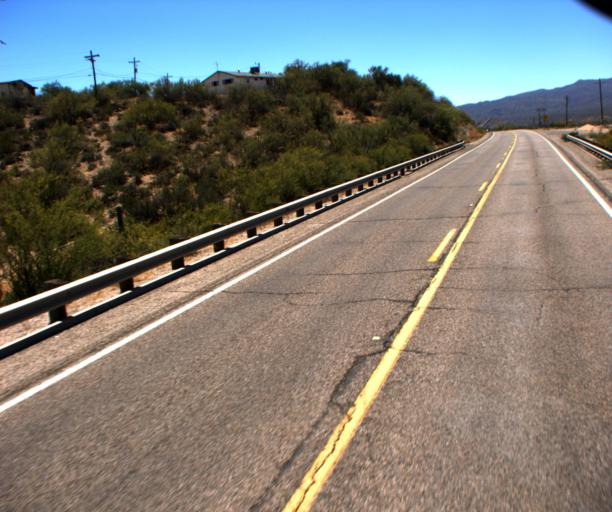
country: US
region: Arizona
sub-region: Pinal County
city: Kearny
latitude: 33.0796
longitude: -110.9245
